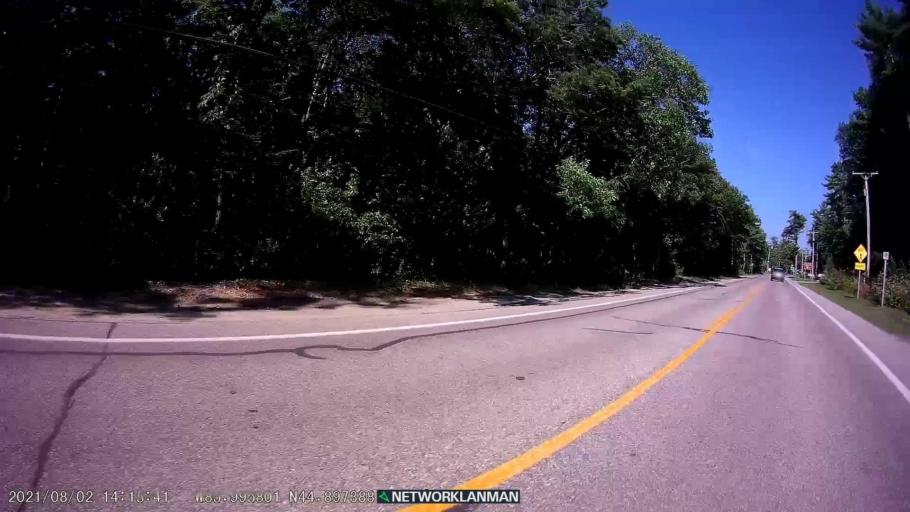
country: US
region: Michigan
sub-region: Leelanau County
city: Leland
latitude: 44.8974
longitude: -85.9956
